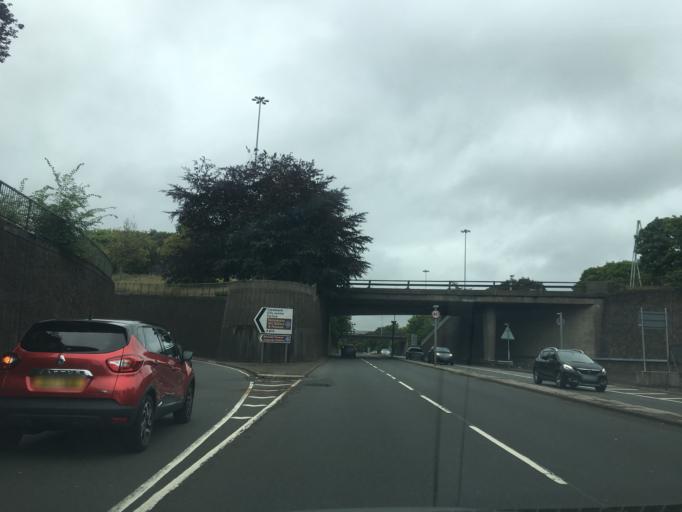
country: GB
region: Scotland
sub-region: East Dunbartonshire
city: Bearsden
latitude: 55.8729
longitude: -4.3294
